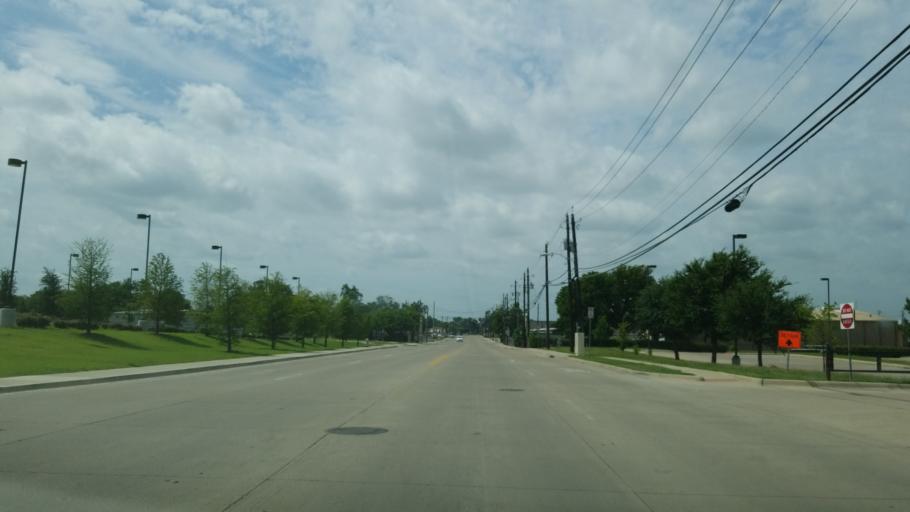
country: US
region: Texas
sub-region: Dallas County
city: Farmers Branch
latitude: 32.8725
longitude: -96.8754
